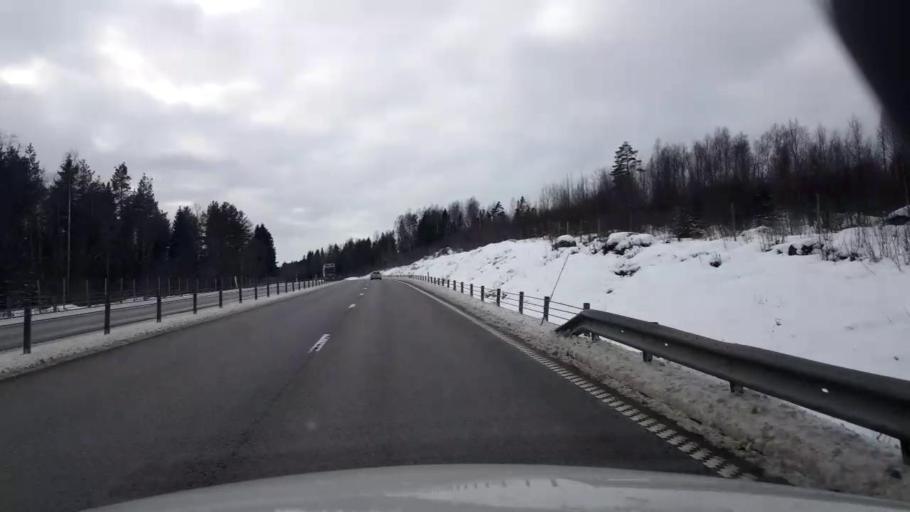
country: SE
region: Vaesternorrland
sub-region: Sundsvalls Kommun
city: Njurundabommen
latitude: 62.0838
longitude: 17.2870
